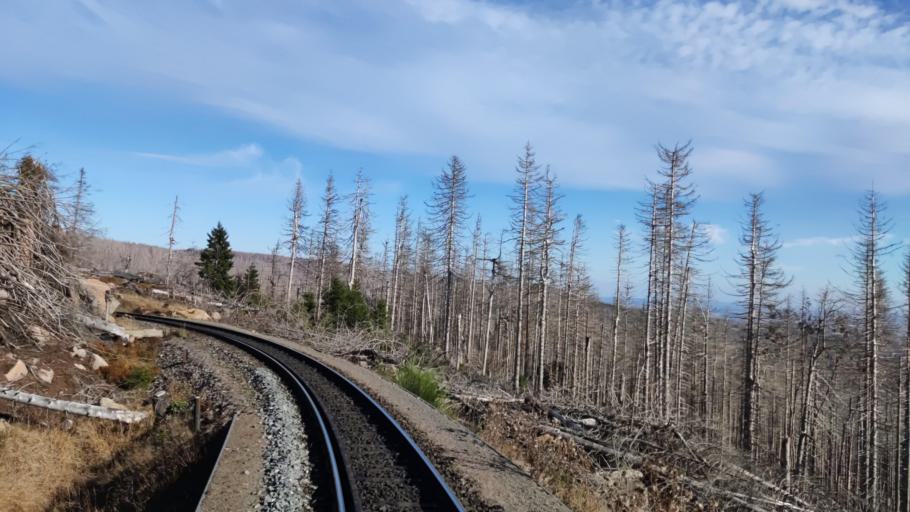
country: DE
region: Lower Saxony
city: Braunlage
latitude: 51.7773
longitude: 10.6218
